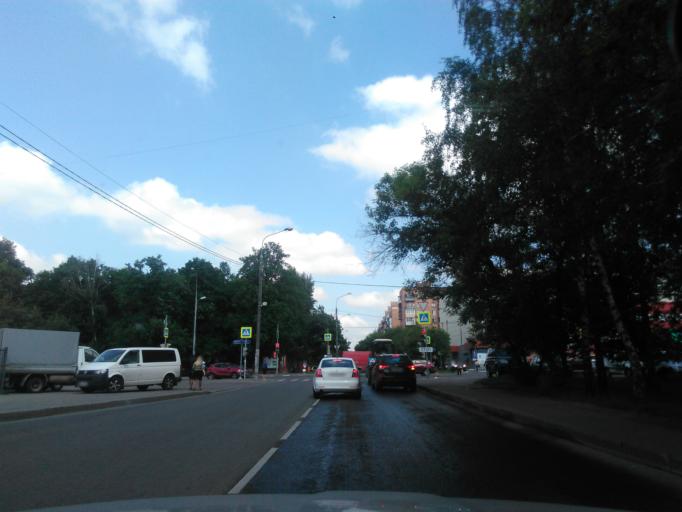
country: RU
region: Moscow
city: Vagonoremont
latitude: 55.8886
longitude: 37.5366
